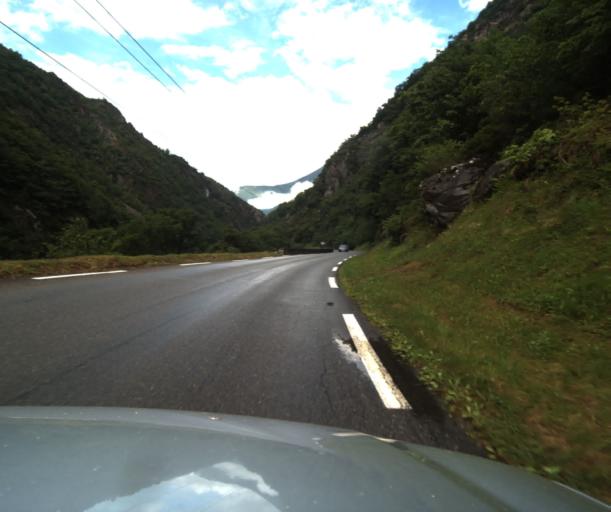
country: FR
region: Midi-Pyrenees
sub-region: Departement des Hautes-Pyrenees
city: Luz-Saint-Sauveur
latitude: 42.8475
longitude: -0.0069
